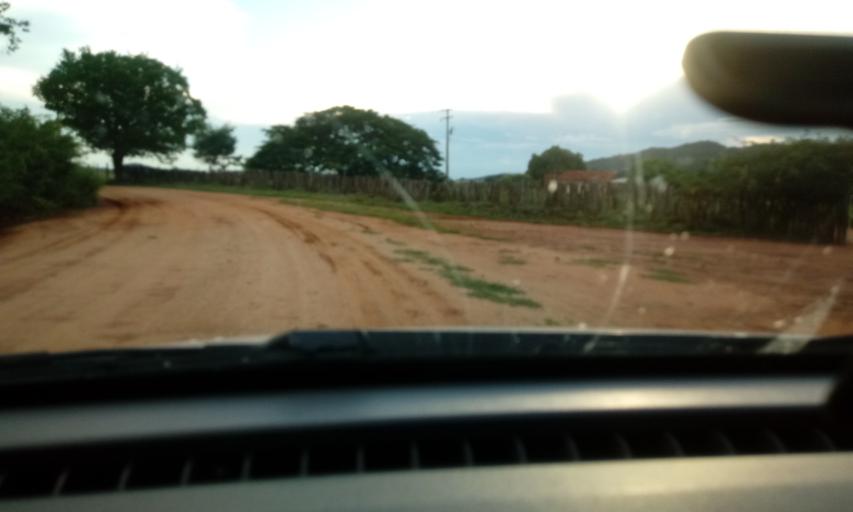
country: BR
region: Bahia
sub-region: Riacho De Santana
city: Riacho de Santana
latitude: -13.8564
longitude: -42.7770
